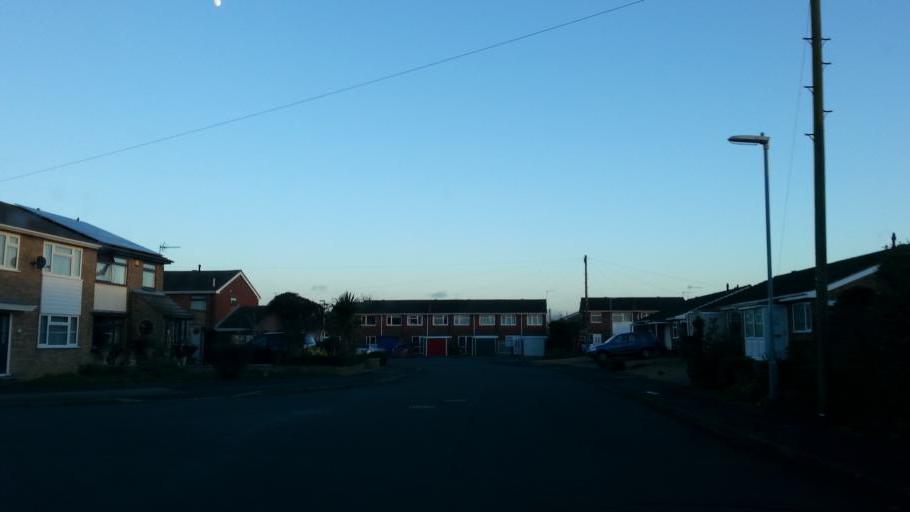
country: GB
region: England
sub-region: Cambridgeshire
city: Hemingford Grey
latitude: 52.2999
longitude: -0.0644
